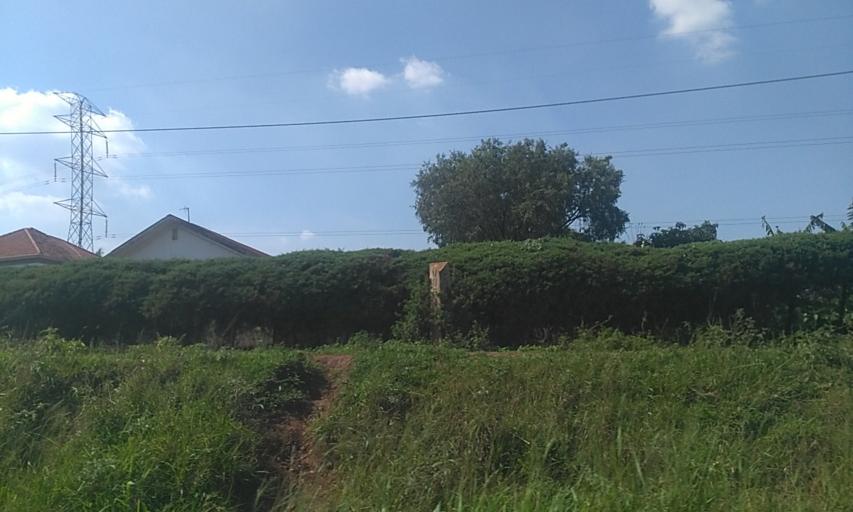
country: UG
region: Central Region
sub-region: Wakiso District
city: Kireka
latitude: 0.3654
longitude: 32.6425
